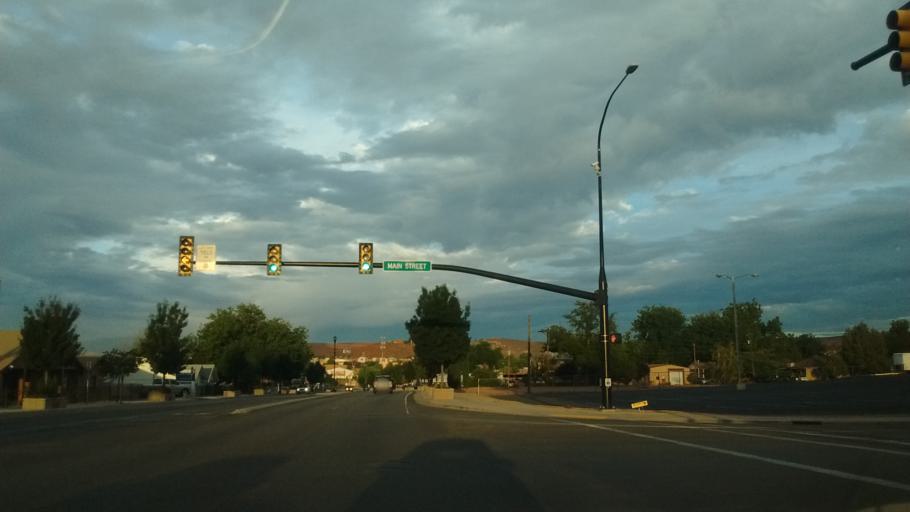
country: US
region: Utah
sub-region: Washington County
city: Washington
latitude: 37.1304
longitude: -113.5098
